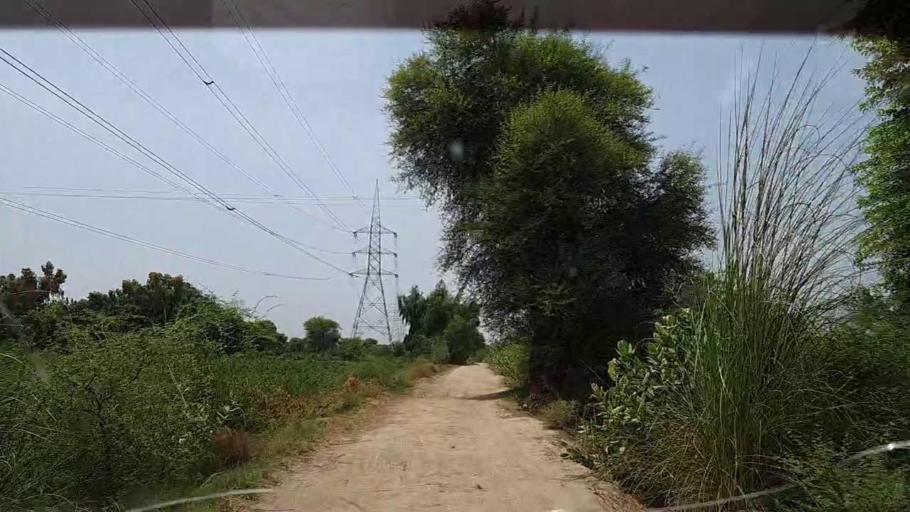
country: PK
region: Sindh
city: Adilpur
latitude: 27.8812
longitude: 69.2623
